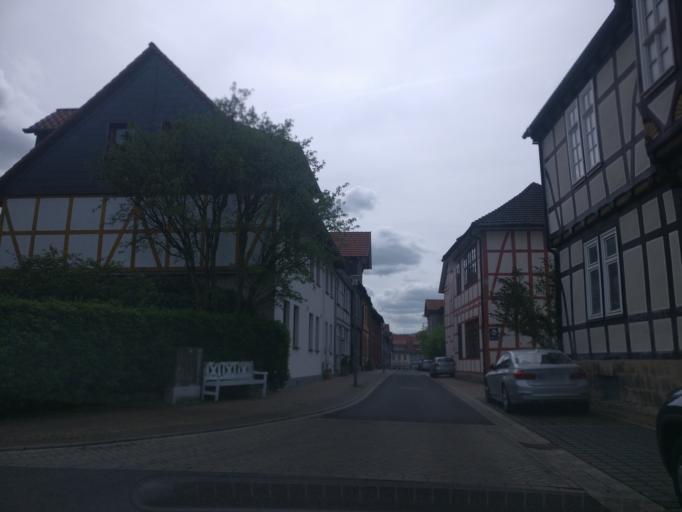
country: DE
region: Lower Saxony
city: Dransfeld
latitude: 51.5043
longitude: 9.7601
